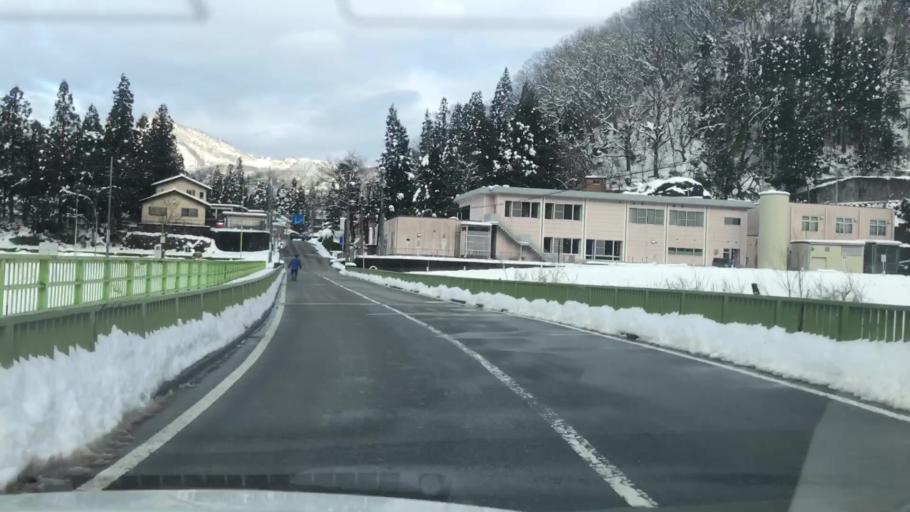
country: JP
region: Toyama
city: Kamiichi
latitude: 36.5702
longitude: 137.3816
